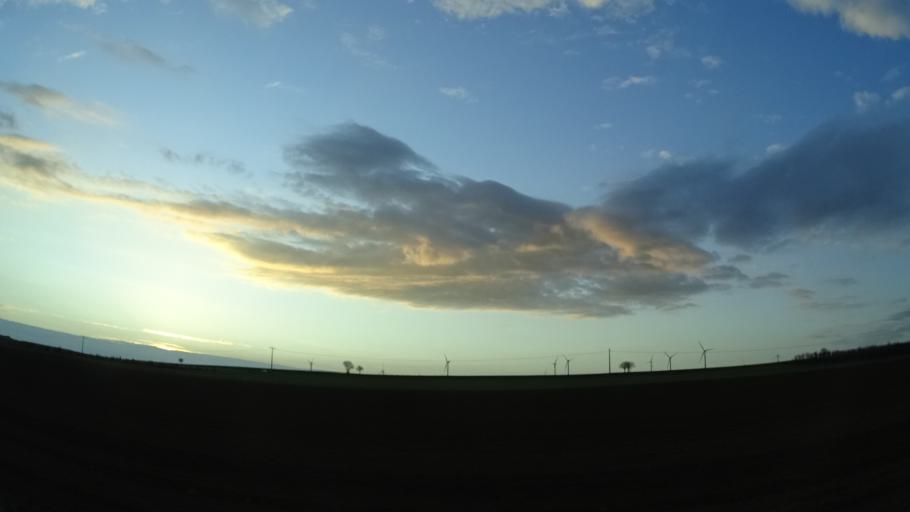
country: DE
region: Rheinland-Pfalz
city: Flonheim
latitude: 49.7944
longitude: 8.0476
